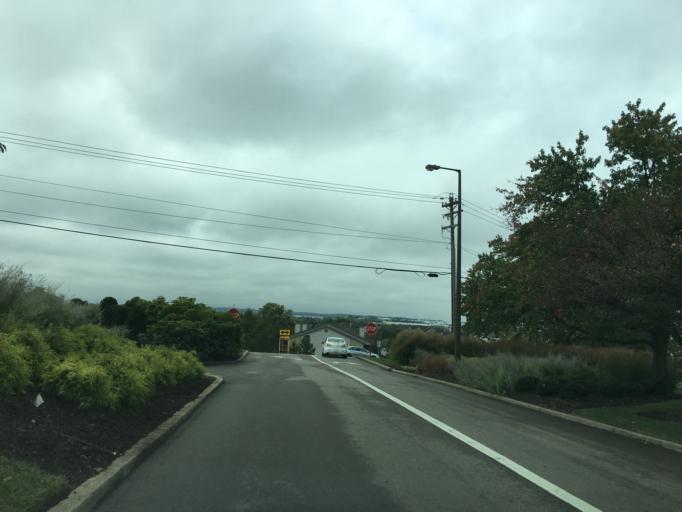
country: US
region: Ohio
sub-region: Butler County
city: Beckett Ridge
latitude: 39.3513
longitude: -84.4507
